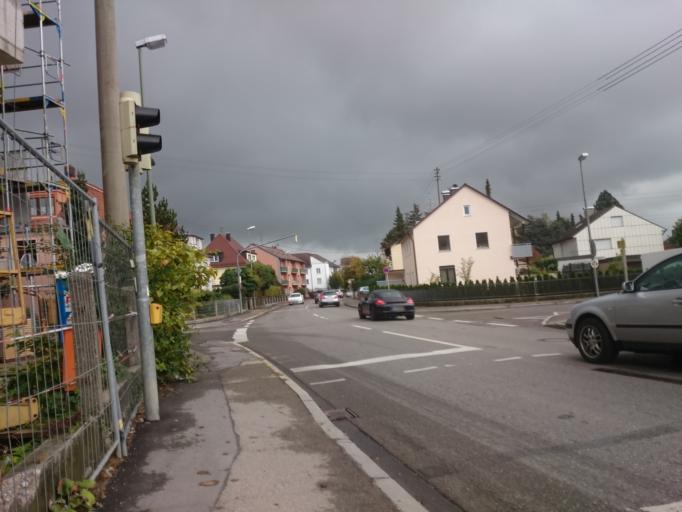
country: DE
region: Bavaria
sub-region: Swabia
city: Gersthofen
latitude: 48.4254
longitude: 10.8718
